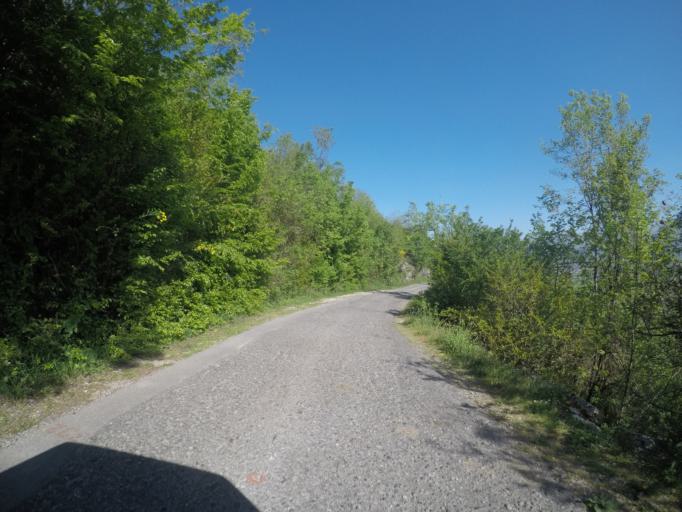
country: ME
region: Danilovgrad
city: Danilovgrad
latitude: 42.5168
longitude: 19.0978
